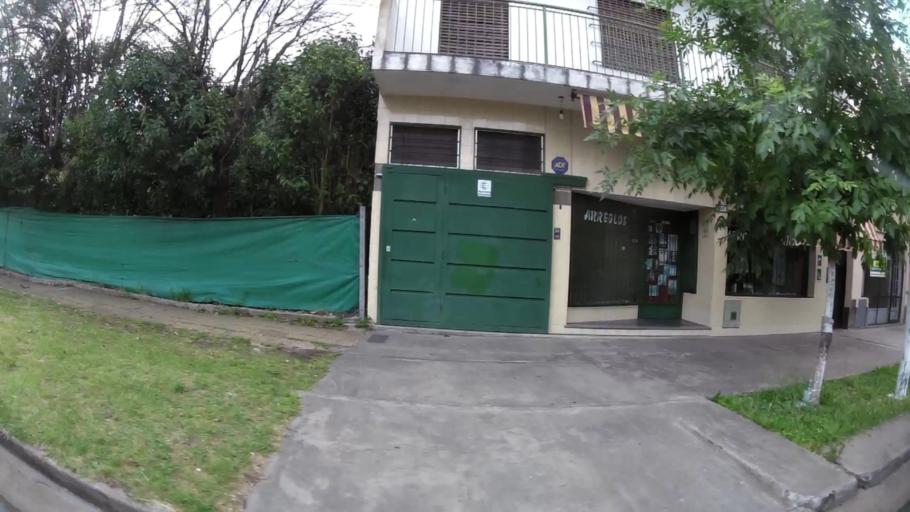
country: AR
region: Buenos Aires
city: Ituzaingo
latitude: -34.6413
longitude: -58.6627
